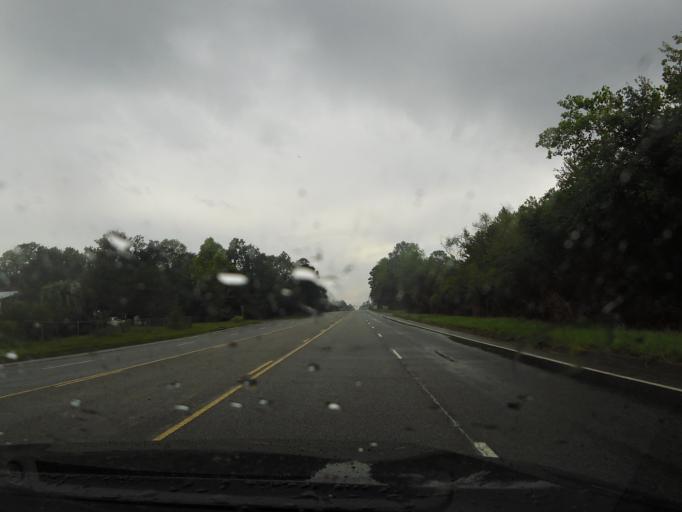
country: US
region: Georgia
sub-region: Wayne County
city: Jesup
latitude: 31.5906
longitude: -81.8653
